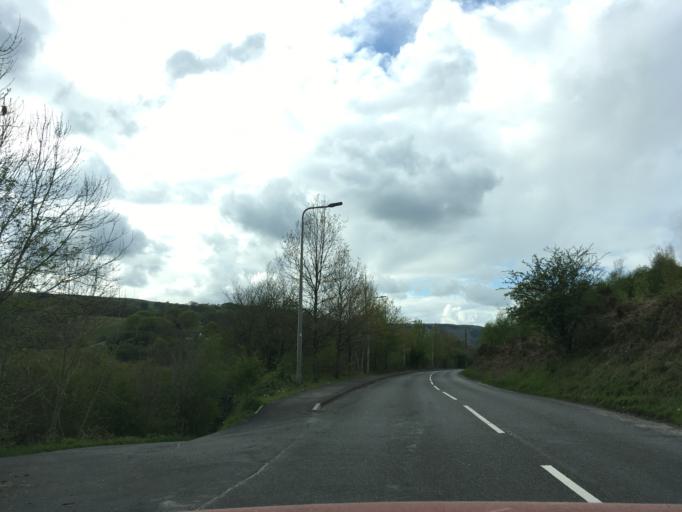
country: GB
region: Wales
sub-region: Merthyr Tydfil County Borough
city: Treharris
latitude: 51.6924
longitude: -3.3033
